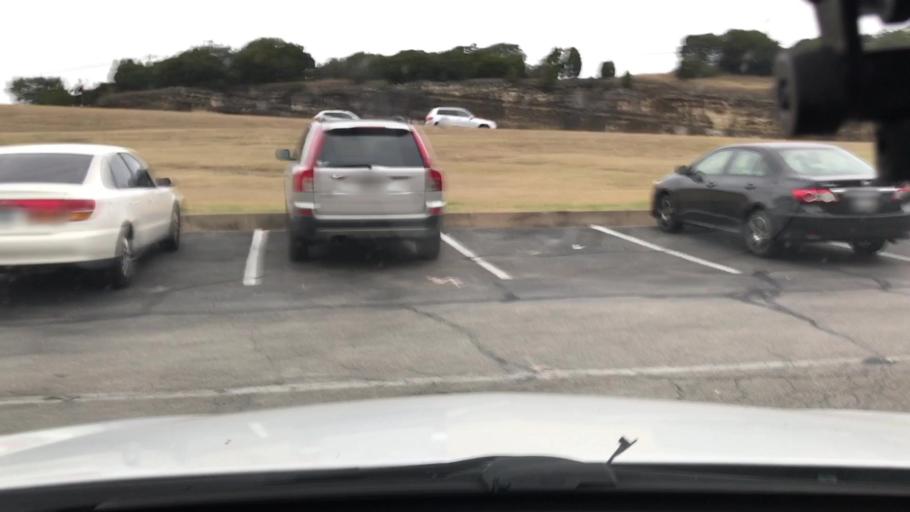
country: US
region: Texas
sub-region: Williamson County
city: Jollyville
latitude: 30.3858
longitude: -97.7646
